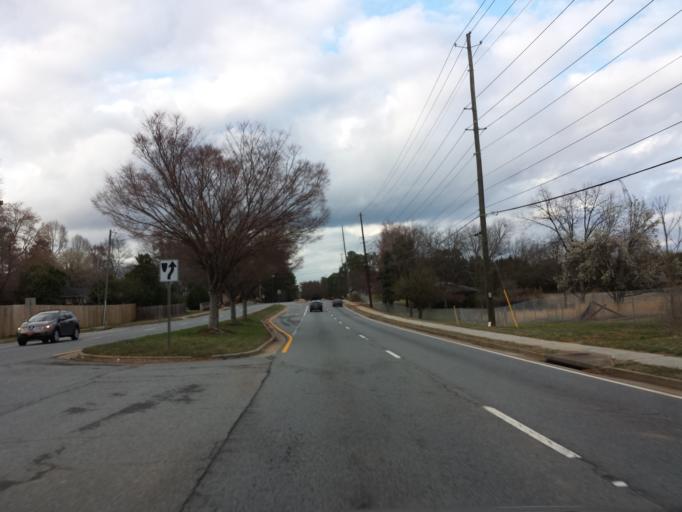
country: US
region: Georgia
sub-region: Cobb County
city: Vinings
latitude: 33.9308
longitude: -84.4609
